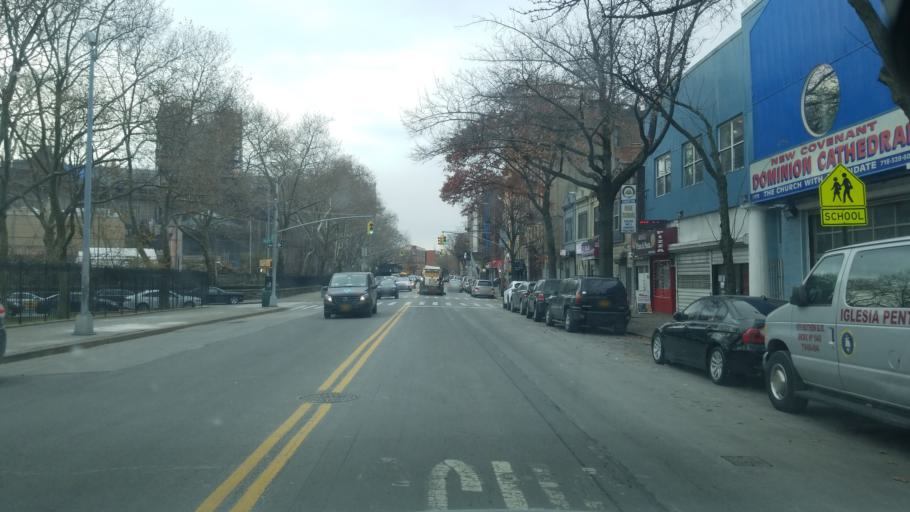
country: US
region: New York
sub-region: Bronx
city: The Bronx
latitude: 40.8290
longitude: -73.9030
